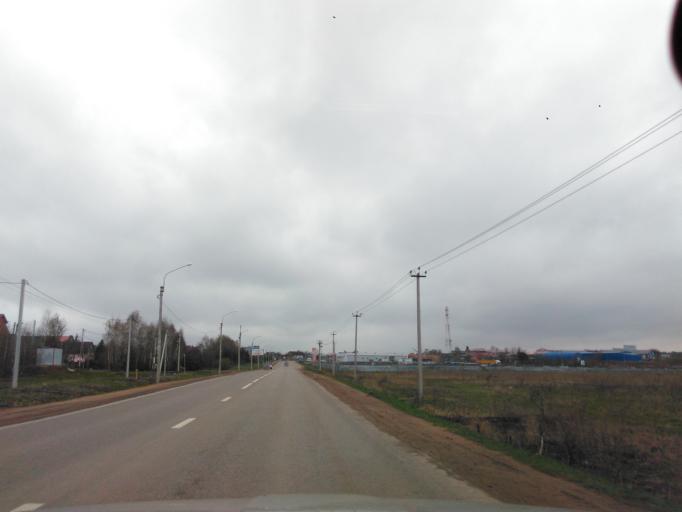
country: RU
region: Moskovskaya
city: Pavlovskaya Sloboda
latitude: 55.8180
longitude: 37.0666
